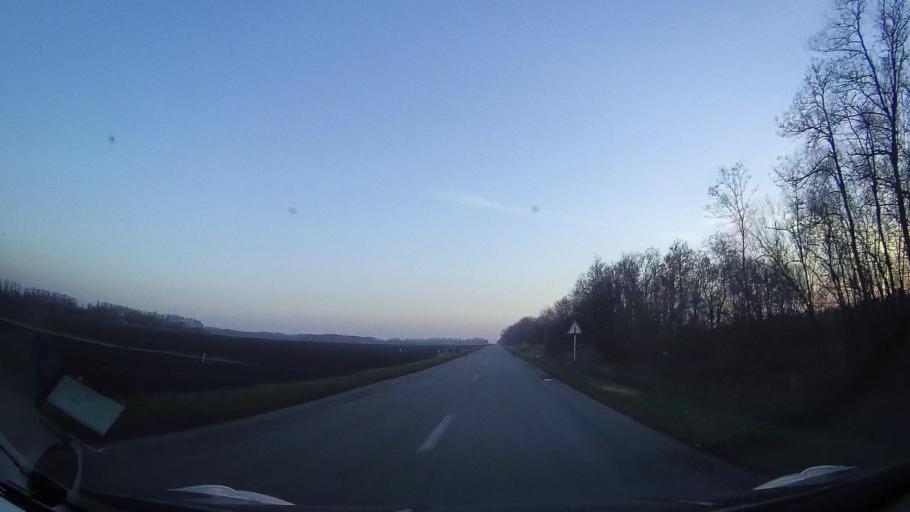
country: RU
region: Rostov
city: Zernograd
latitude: 47.0032
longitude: 40.3915
